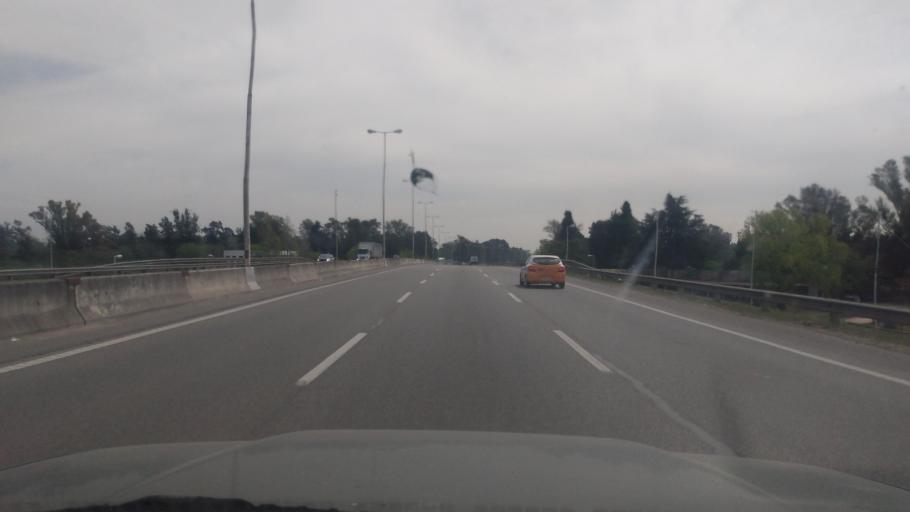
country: AR
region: Buenos Aires
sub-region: Partido de Pilar
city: Pilar
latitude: -34.4313
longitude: -58.9926
